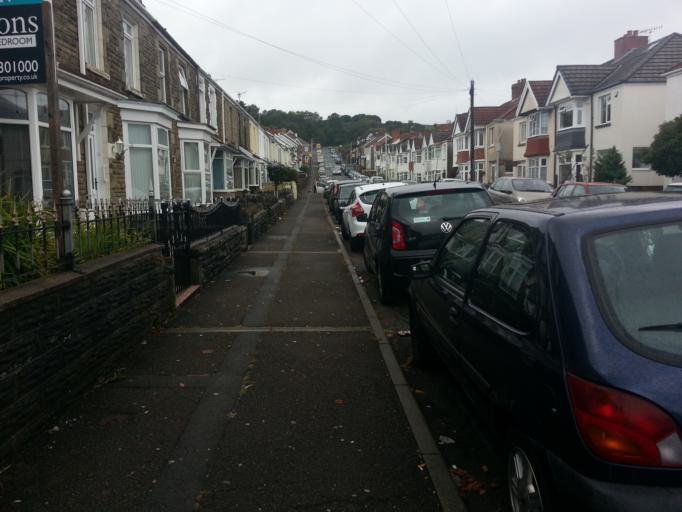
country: GB
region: Wales
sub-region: City and County of Swansea
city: Landore
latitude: 51.6415
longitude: -3.9515
